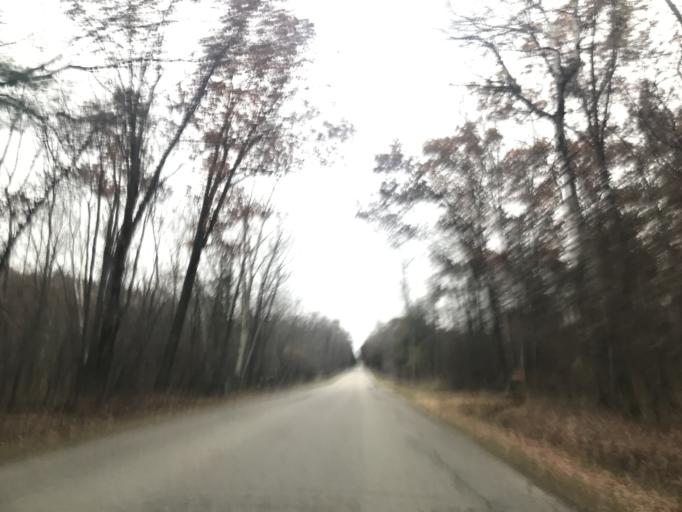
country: US
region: Wisconsin
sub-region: Marinette County
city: Peshtigo
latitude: 45.1195
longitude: -87.7499
